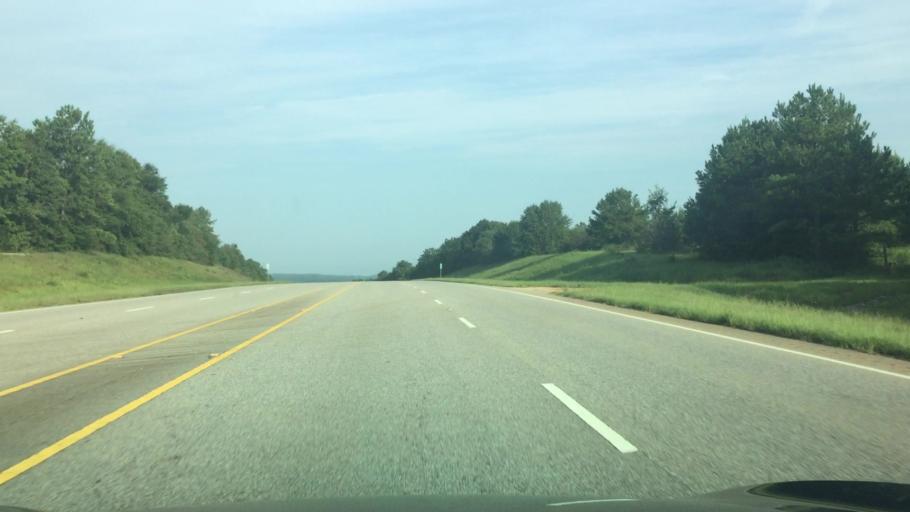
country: US
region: Alabama
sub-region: Butler County
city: Georgiana
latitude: 31.4609
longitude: -86.6434
